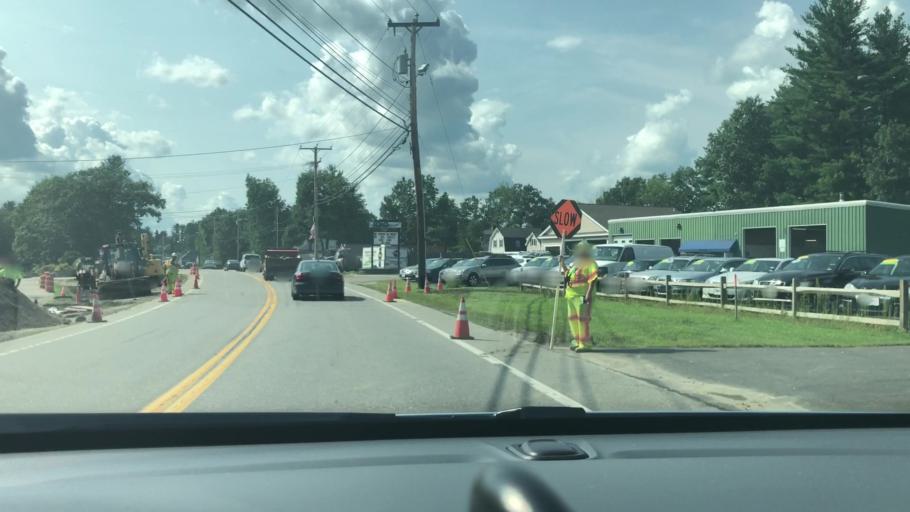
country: US
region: New Hampshire
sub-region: Hillsborough County
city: Pinardville
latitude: 43.0117
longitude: -71.5470
